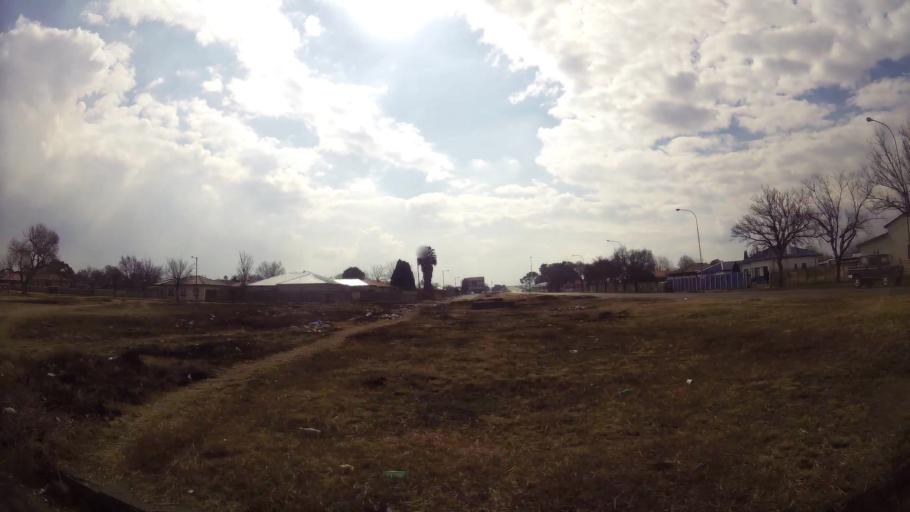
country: ZA
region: Gauteng
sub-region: Sedibeng District Municipality
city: Vereeniging
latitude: -26.6672
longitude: 27.9194
